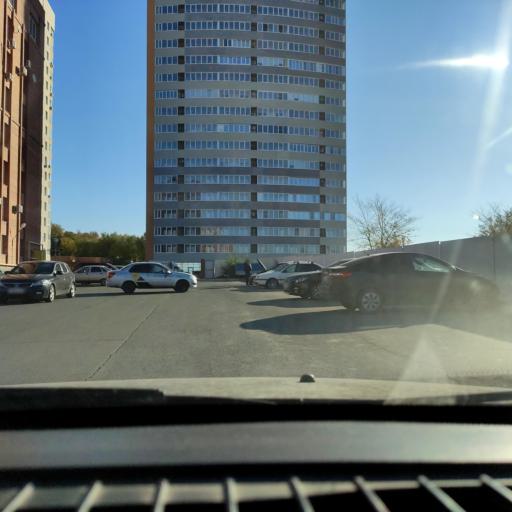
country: RU
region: Samara
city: Tol'yatti
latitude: 53.5056
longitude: 49.2507
